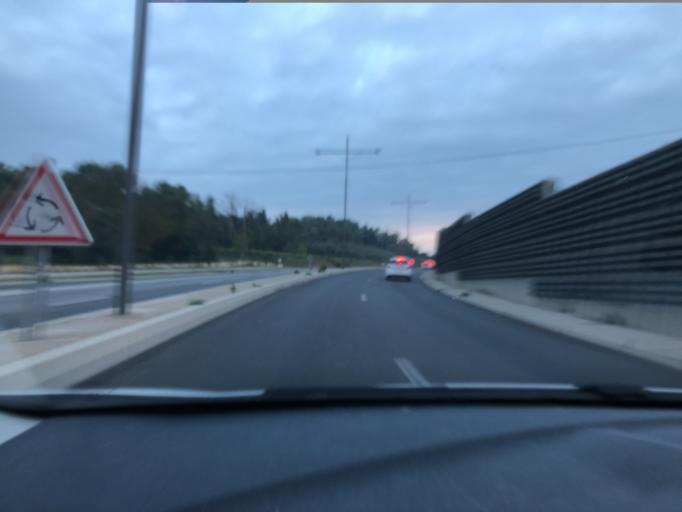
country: FR
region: Languedoc-Roussillon
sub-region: Departement de l'Herault
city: Montferrier-sur-Lez
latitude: 43.6465
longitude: 3.8541
